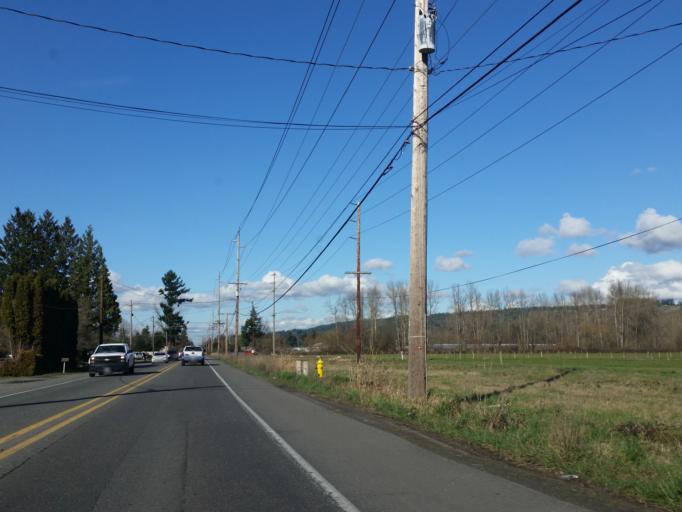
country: US
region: Washington
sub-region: Pierce County
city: Alderton
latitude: 47.1819
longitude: -122.2293
